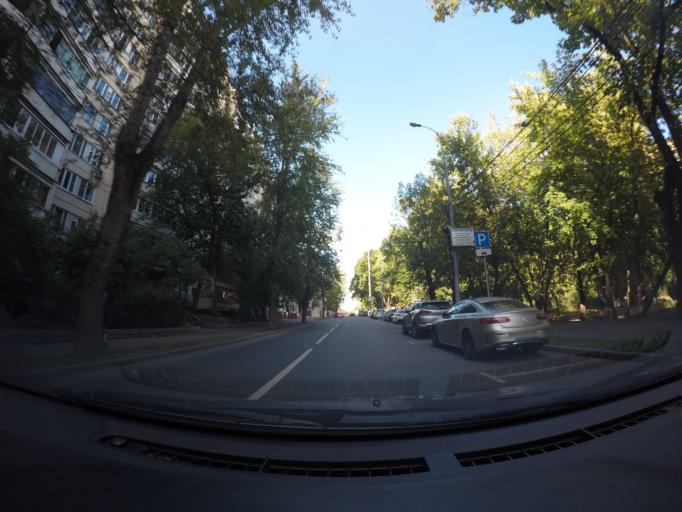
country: RU
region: Moscow
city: Sokol'niki
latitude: 55.7949
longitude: 37.6929
